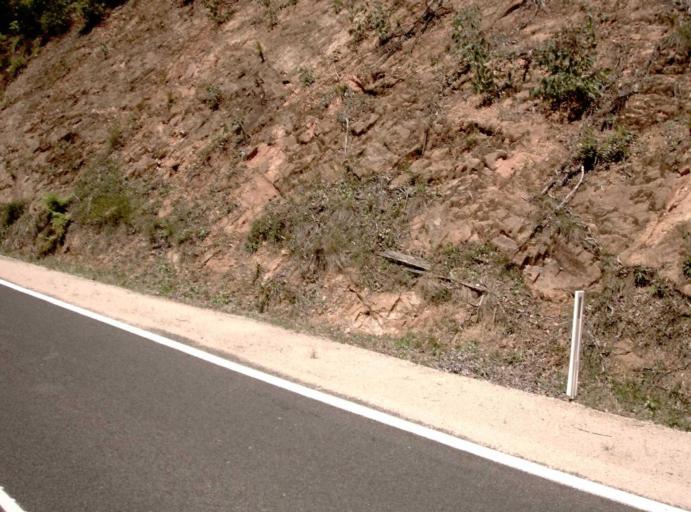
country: AU
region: New South Wales
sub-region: Bombala
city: Bombala
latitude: -37.5920
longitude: 148.9892
